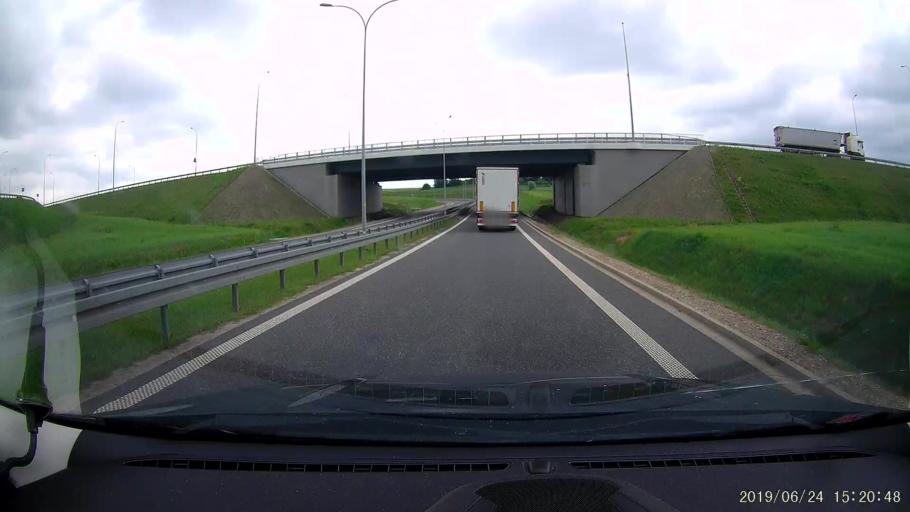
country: PL
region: Subcarpathian Voivodeship
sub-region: Powiat przeworski
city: Mirocin
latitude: 50.0383
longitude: 22.5774
